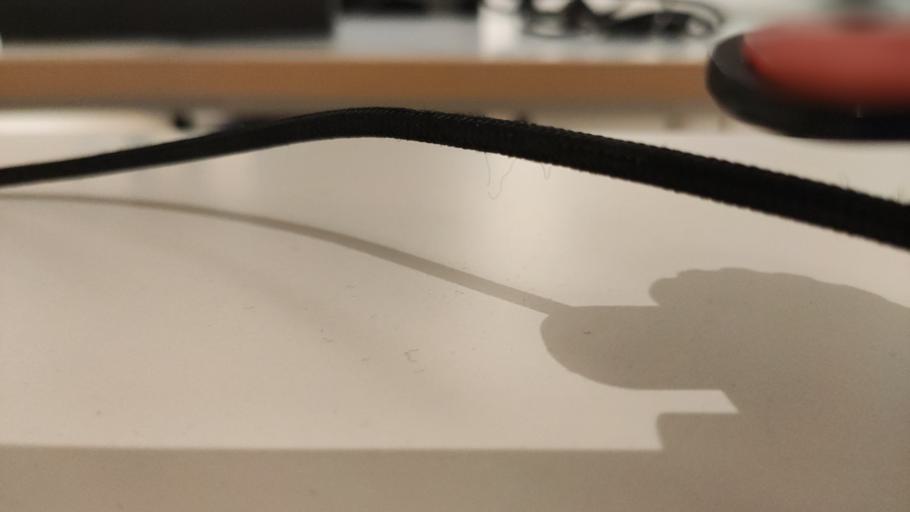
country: RU
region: Moskovskaya
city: Dorokhovo
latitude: 55.4636
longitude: 36.3546
